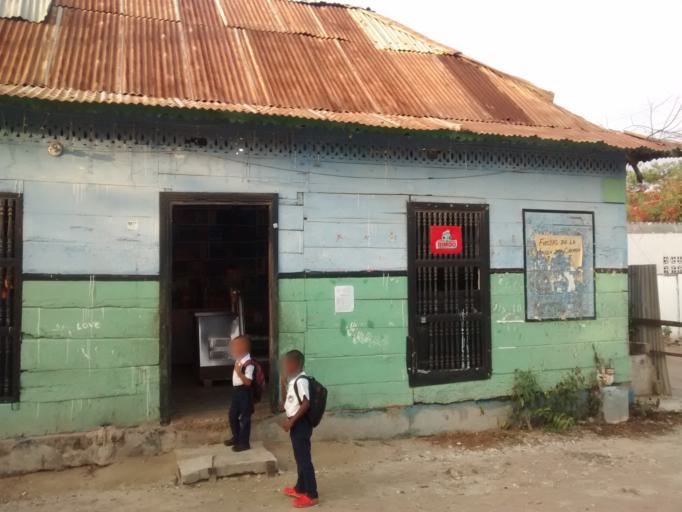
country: CO
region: Bolivar
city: Turbana
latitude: 10.1415
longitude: -75.6855
